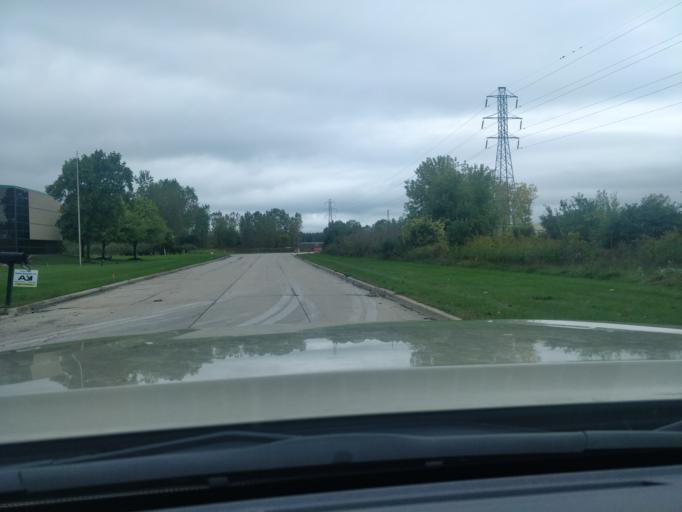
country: US
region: Michigan
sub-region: Wayne County
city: Romulus
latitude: 42.1757
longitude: -83.3898
